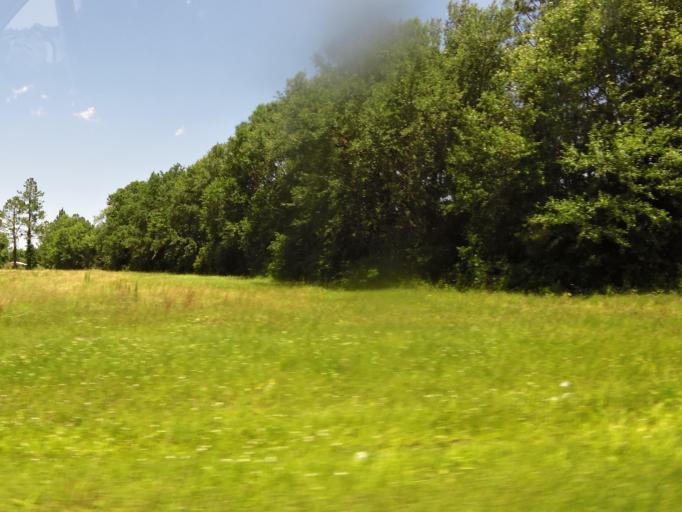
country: US
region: Florida
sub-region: Bradford County
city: Starke
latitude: 30.0180
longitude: -82.2011
